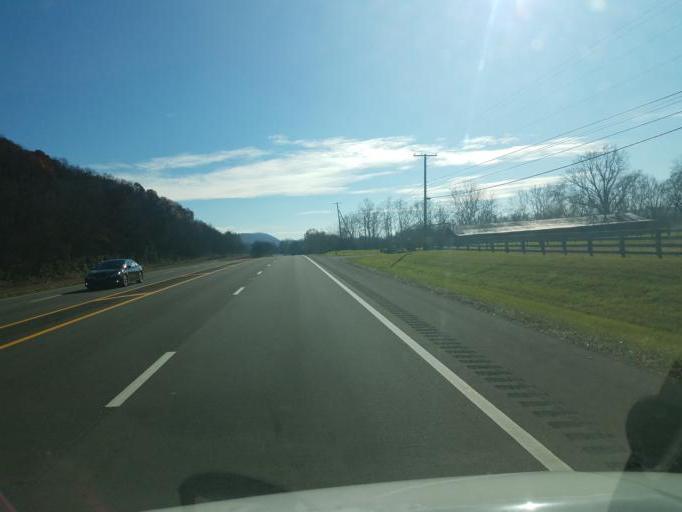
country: US
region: Ohio
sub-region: Scioto County
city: Lucasville
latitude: 38.8514
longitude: -82.9867
